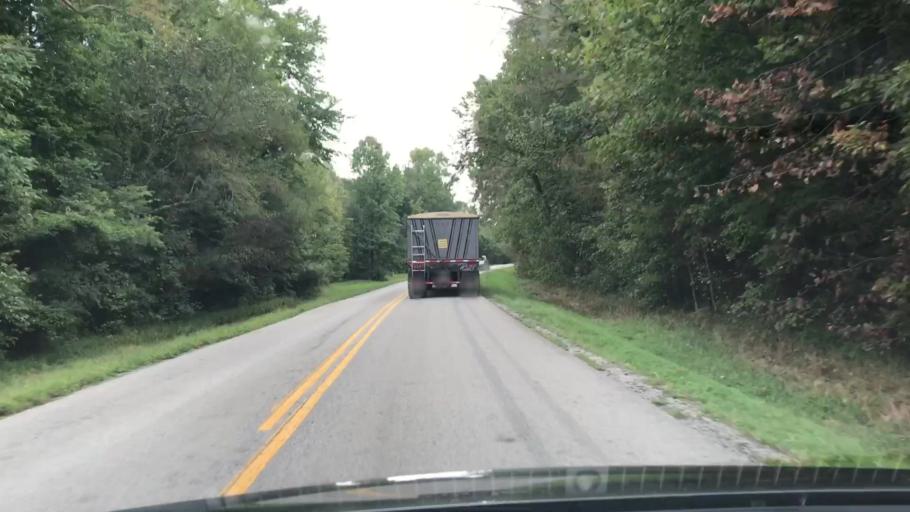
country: US
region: Kentucky
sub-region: Todd County
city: Guthrie
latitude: 36.6823
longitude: -87.0236
